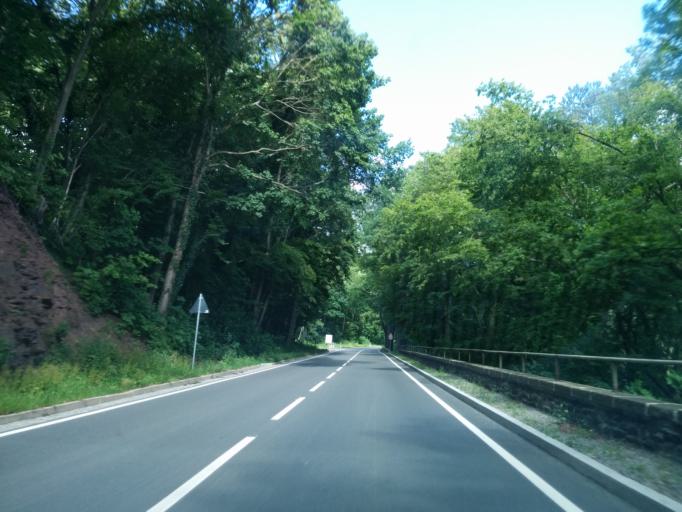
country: DE
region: Saxony
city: Falkenau
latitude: 50.8579
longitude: 13.1171
